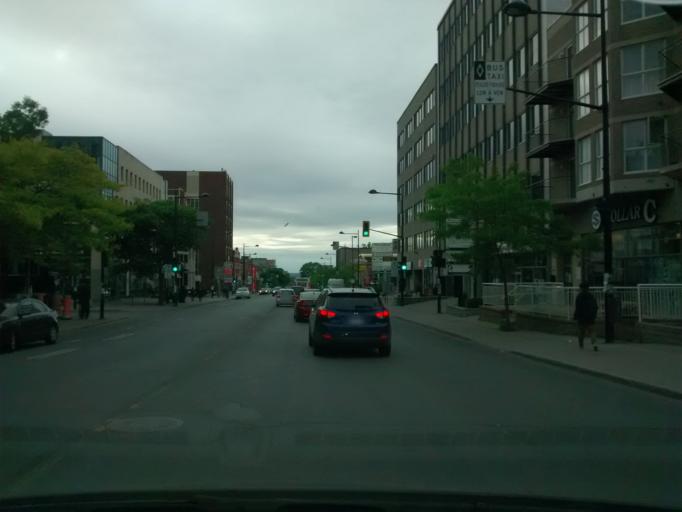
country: CA
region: Quebec
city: Mont-Royal
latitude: 45.4997
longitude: -73.6294
